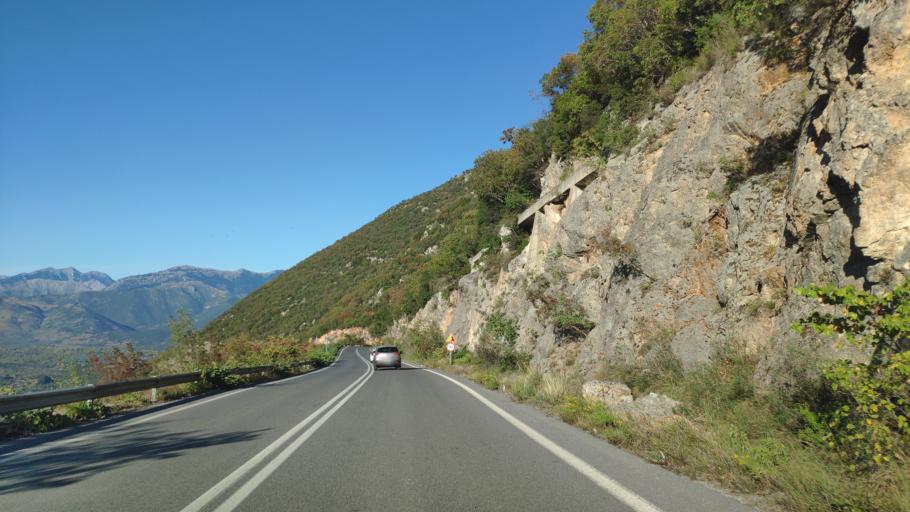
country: GR
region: Peloponnese
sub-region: Nomos Arkadias
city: Langadhia
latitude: 37.7154
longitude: 22.1990
